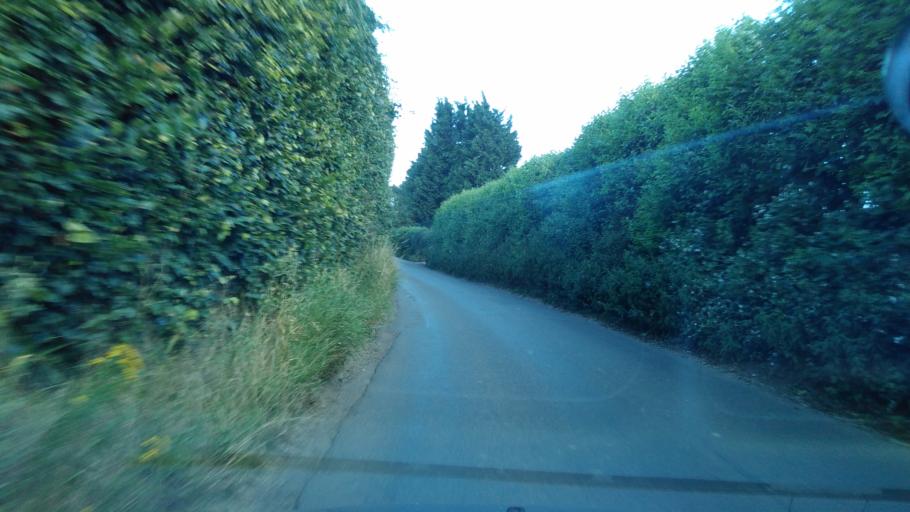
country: GB
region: England
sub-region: Kent
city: Dunkirk
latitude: 51.2700
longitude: 0.9444
